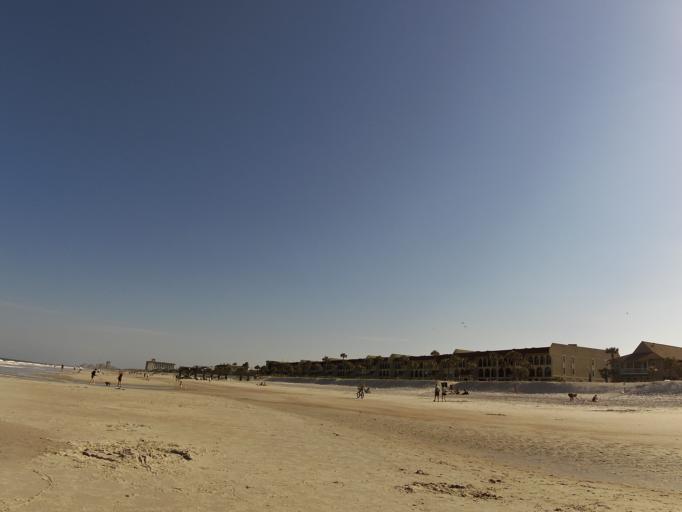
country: US
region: Florida
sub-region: Duval County
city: Atlantic Beach
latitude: 30.3361
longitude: -81.3951
